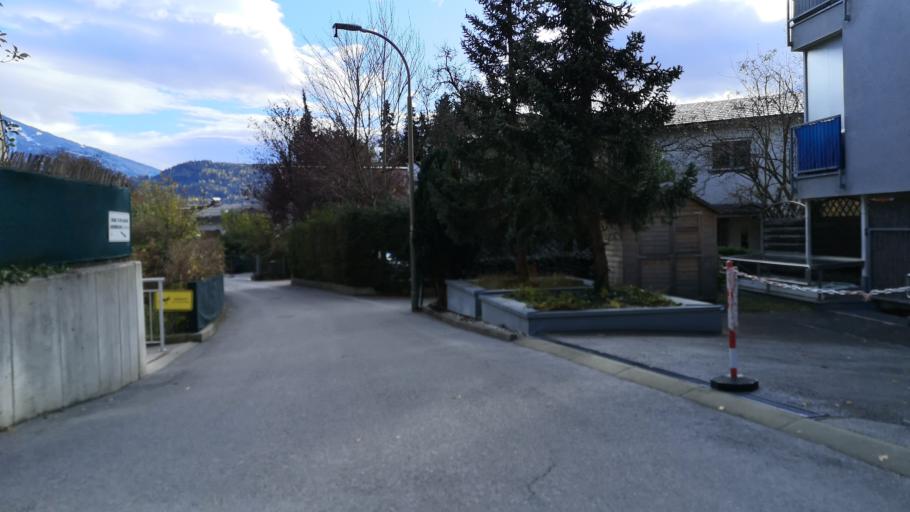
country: AT
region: Tyrol
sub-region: Innsbruck Stadt
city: Innsbruck
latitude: 47.2668
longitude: 11.3641
